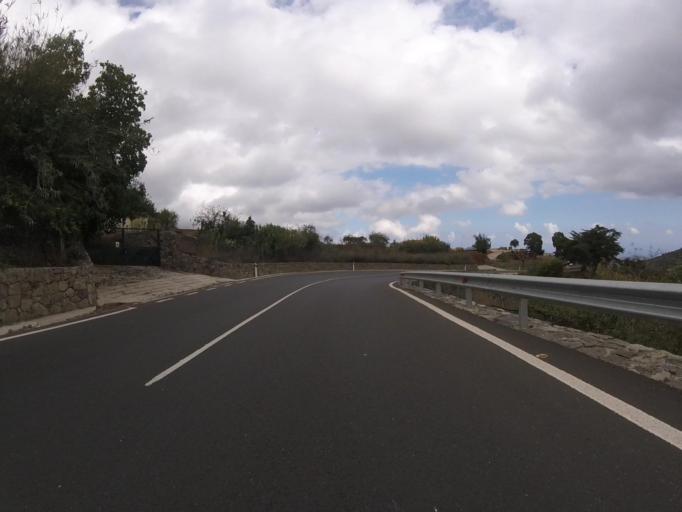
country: ES
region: Canary Islands
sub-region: Provincia de Las Palmas
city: Vega de San Mateo
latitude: 28.0079
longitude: -15.5509
